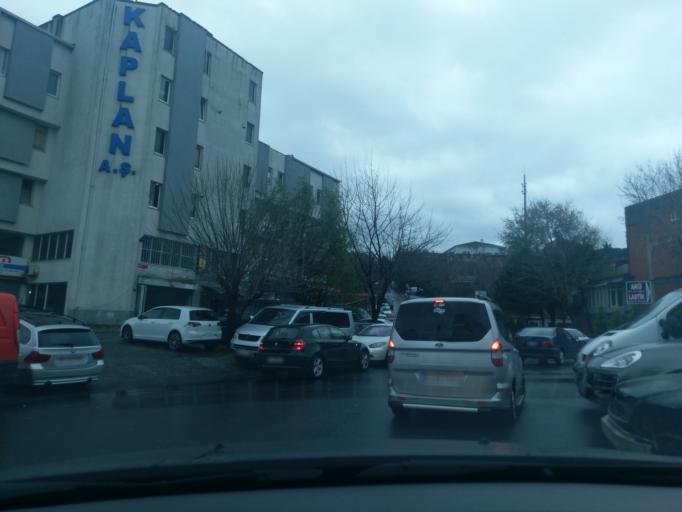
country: TR
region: Istanbul
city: Sisli
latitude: 41.1161
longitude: 29.0179
